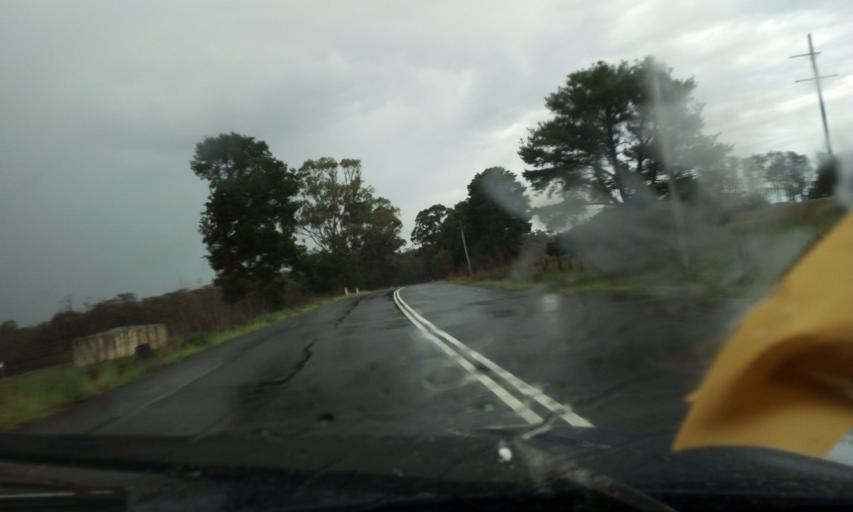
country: AU
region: New South Wales
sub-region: Wollondilly
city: Douglas Park
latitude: -34.2603
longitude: 150.7207
